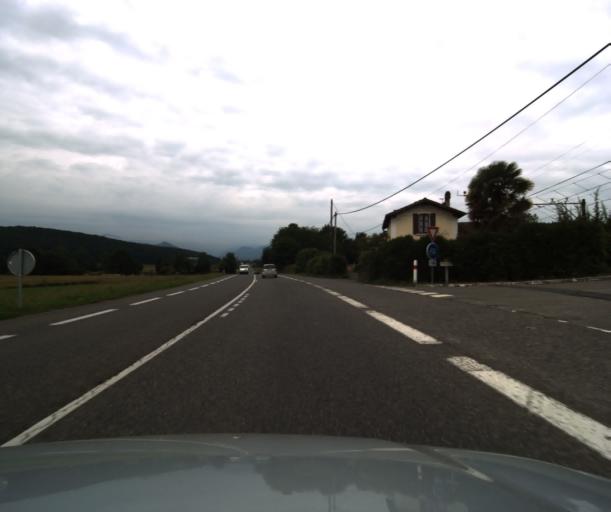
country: FR
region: Midi-Pyrenees
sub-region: Departement des Hautes-Pyrenees
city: Ossun
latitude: 43.1565
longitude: -0.0201
